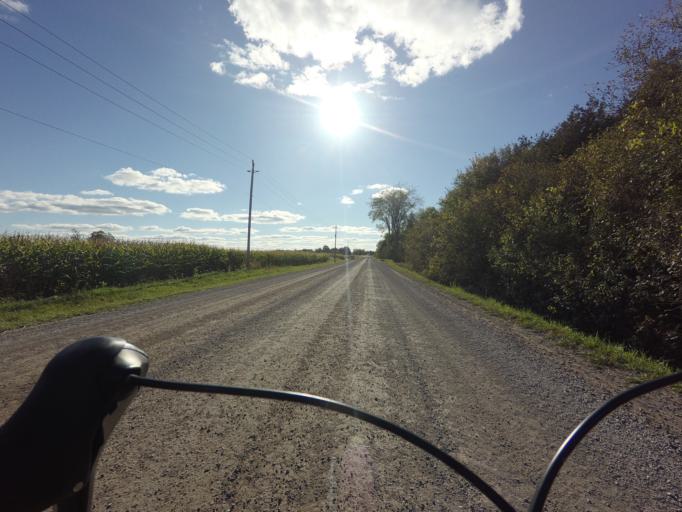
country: CA
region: Ontario
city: Bells Corners
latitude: 45.1099
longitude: -75.7186
